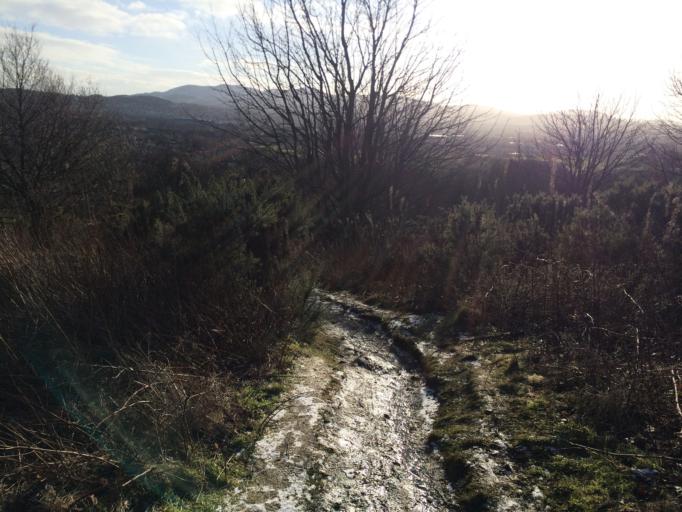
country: GB
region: Scotland
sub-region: Edinburgh
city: Colinton
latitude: 55.9450
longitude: -3.2604
